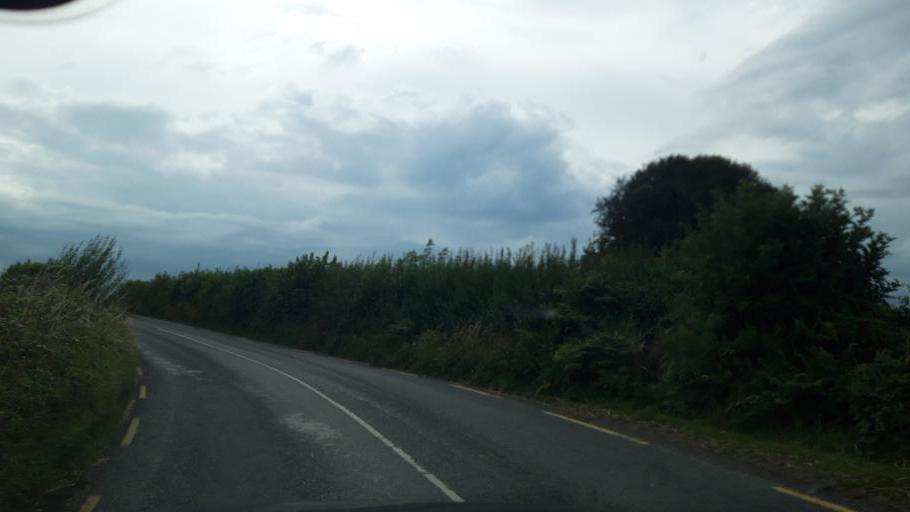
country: IE
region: Leinster
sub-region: Kilkenny
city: Ballyragget
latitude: 52.7619
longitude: -7.3667
